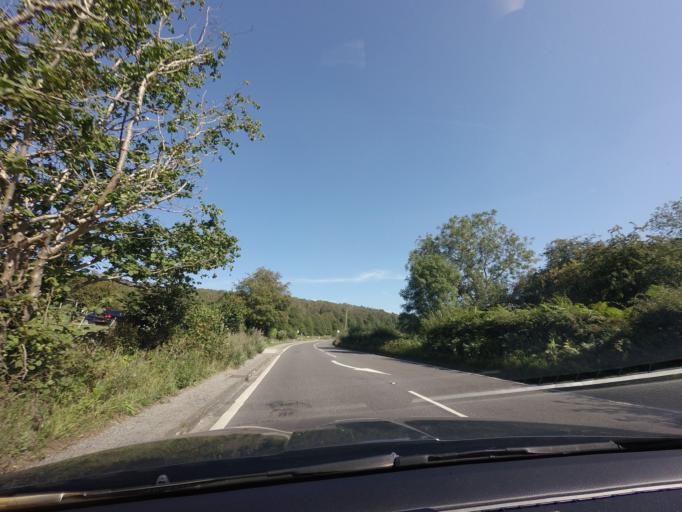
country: GB
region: England
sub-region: Derbyshire
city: Bakewell
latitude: 53.2455
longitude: -1.5847
